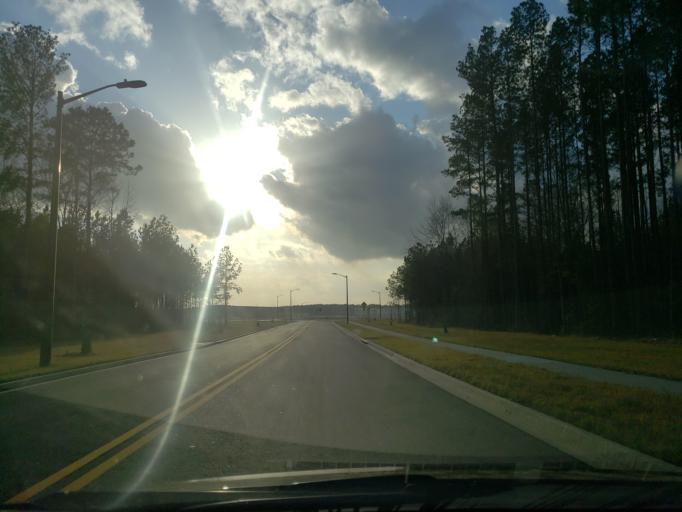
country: US
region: Georgia
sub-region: Chatham County
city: Bloomingdale
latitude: 32.1762
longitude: -81.2659
